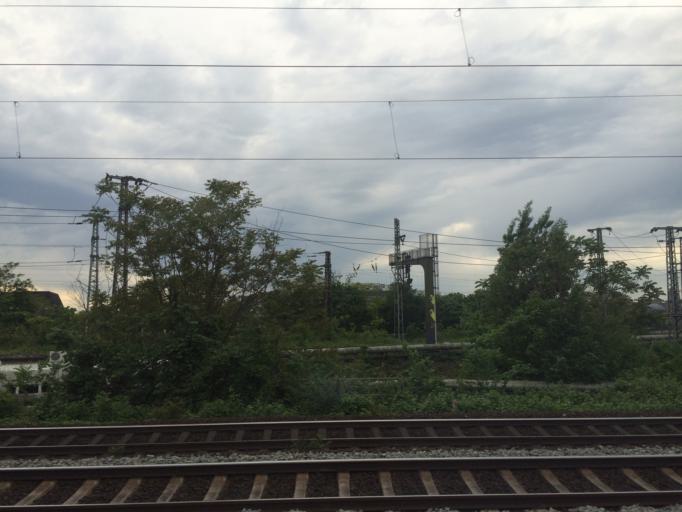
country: DE
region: Hesse
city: Niederrad
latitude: 50.0995
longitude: 8.6504
